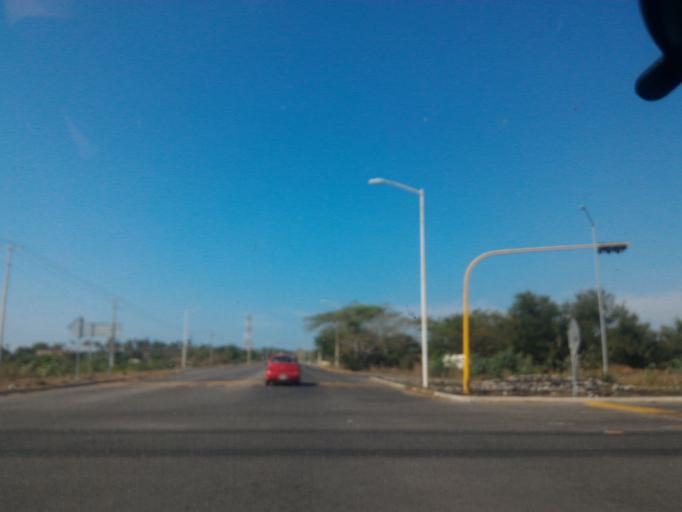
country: MX
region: Colima
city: Tecoman
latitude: 18.9034
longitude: -103.9059
